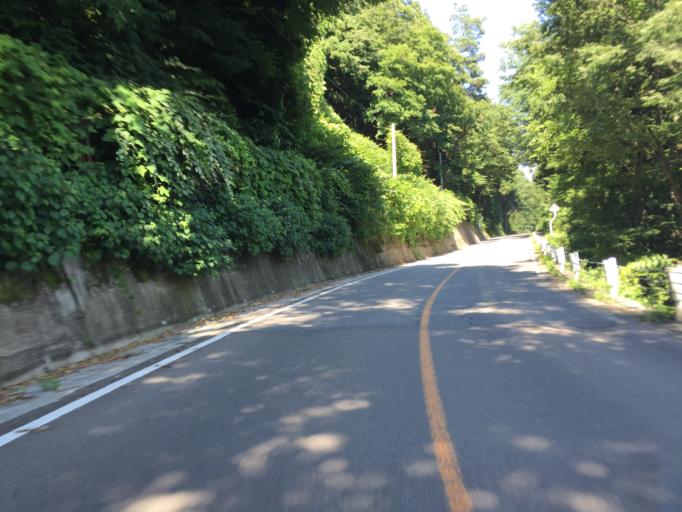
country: JP
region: Fukushima
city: Fukushima-shi
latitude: 37.7537
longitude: 140.3507
